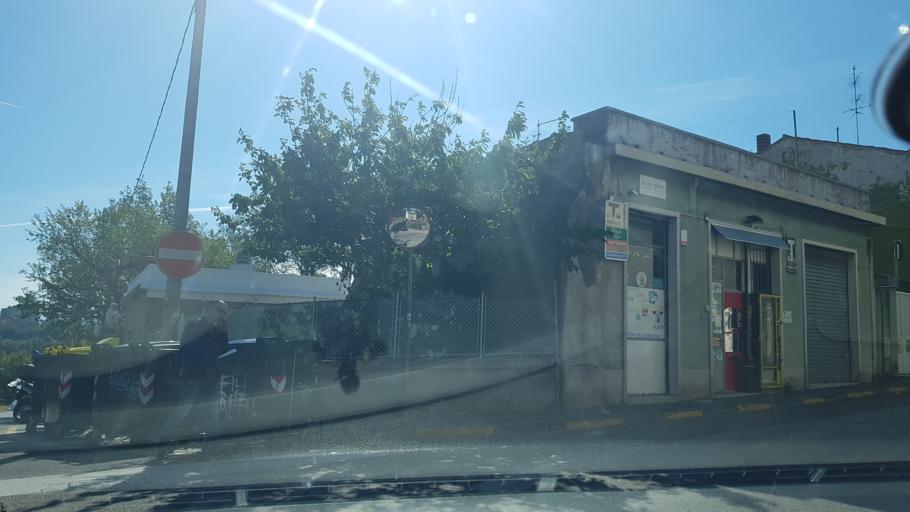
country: IT
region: Friuli Venezia Giulia
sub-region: Provincia di Trieste
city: Trieste
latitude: 45.6308
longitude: 13.7923
